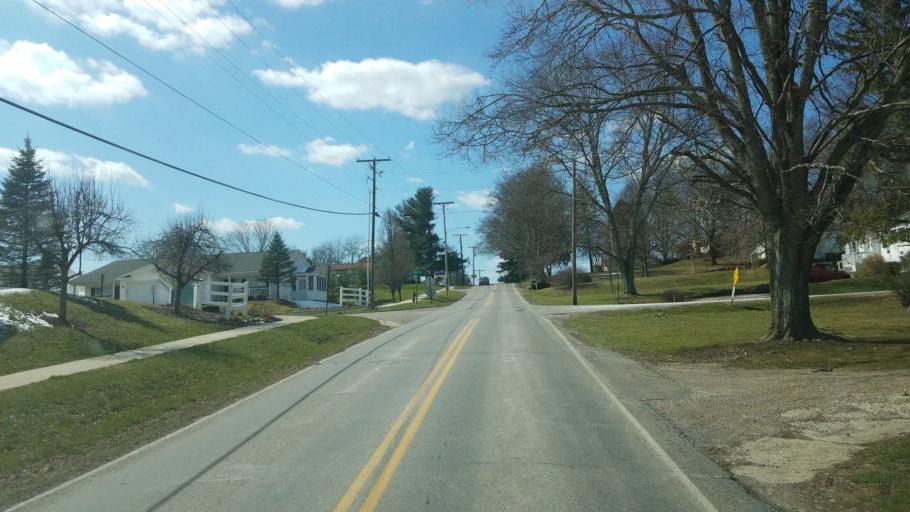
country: US
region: Ohio
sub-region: Knox County
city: Mount Vernon
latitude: 40.4060
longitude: -82.4733
